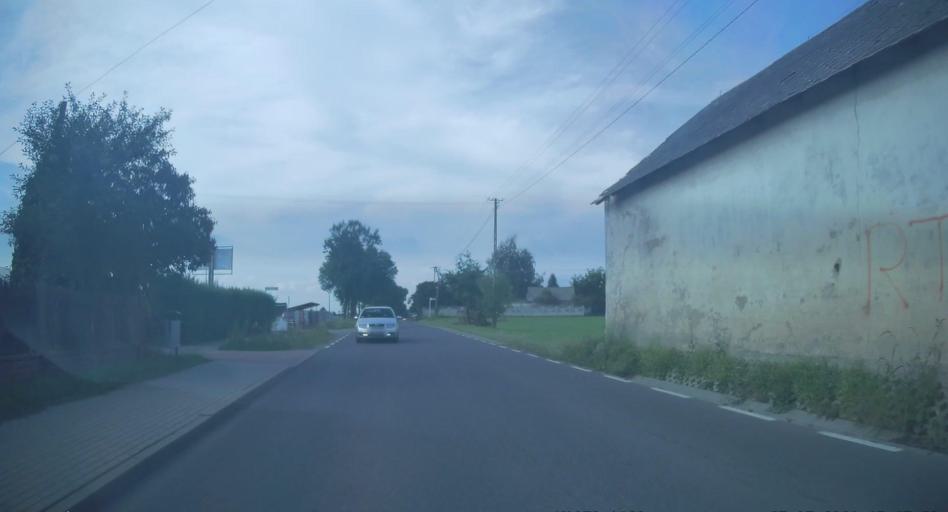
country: PL
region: Lodz Voivodeship
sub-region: Powiat tomaszowski
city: Rzeczyca
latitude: 51.6005
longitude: 20.2939
